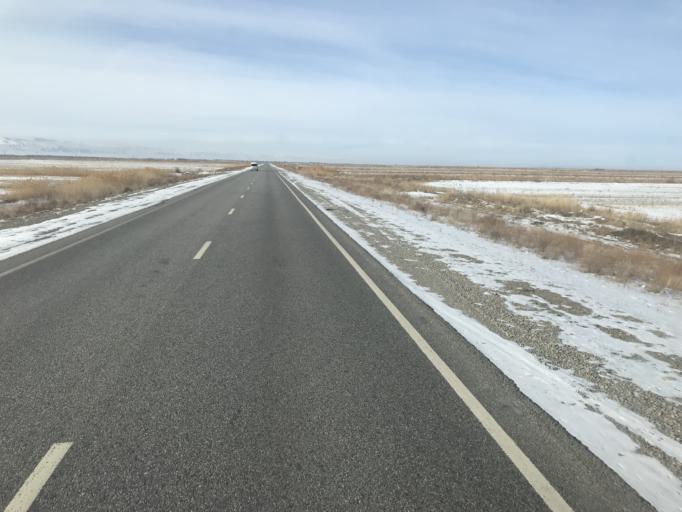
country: KZ
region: Zhambyl
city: Taraz
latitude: 43.0106
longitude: 71.2914
